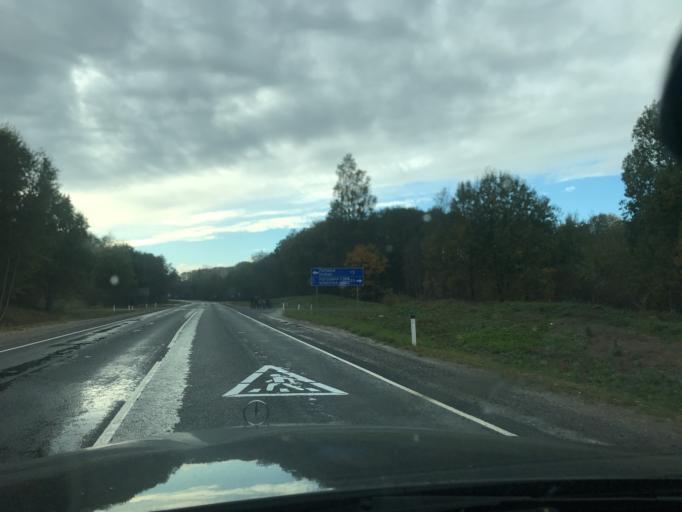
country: RU
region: Pskov
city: Pechory
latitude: 57.6513
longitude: 27.4258
